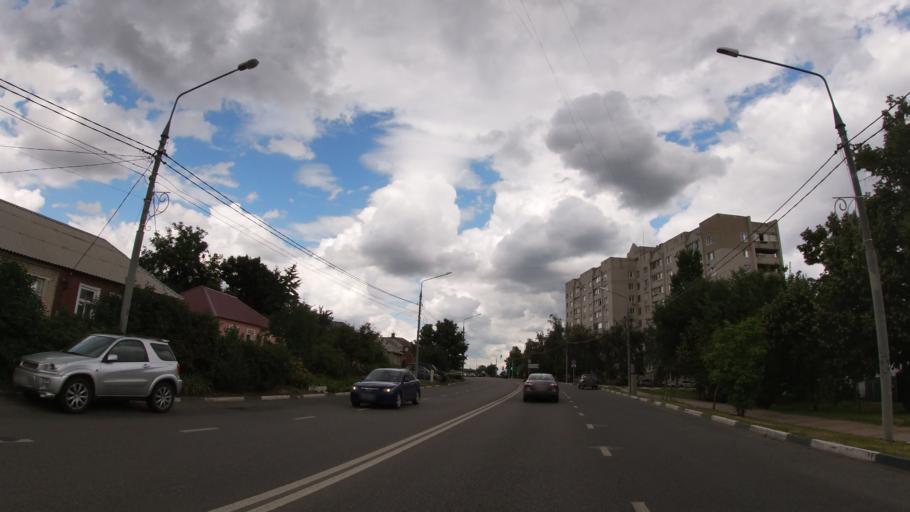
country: RU
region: Belgorod
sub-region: Belgorodskiy Rayon
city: Belgorod
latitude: 50.6015
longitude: 36.6091
